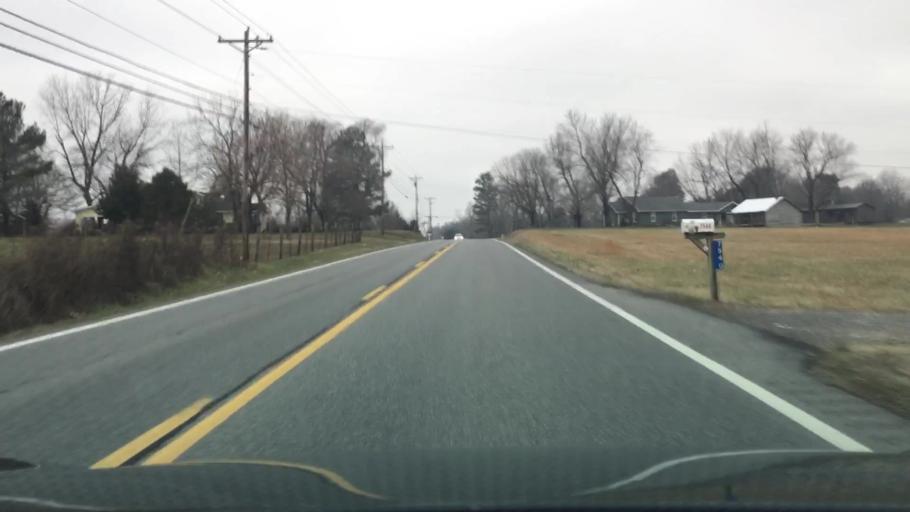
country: US
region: Kentucky
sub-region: McCracken County
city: Reidland
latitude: 36.9834
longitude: -88.4906
